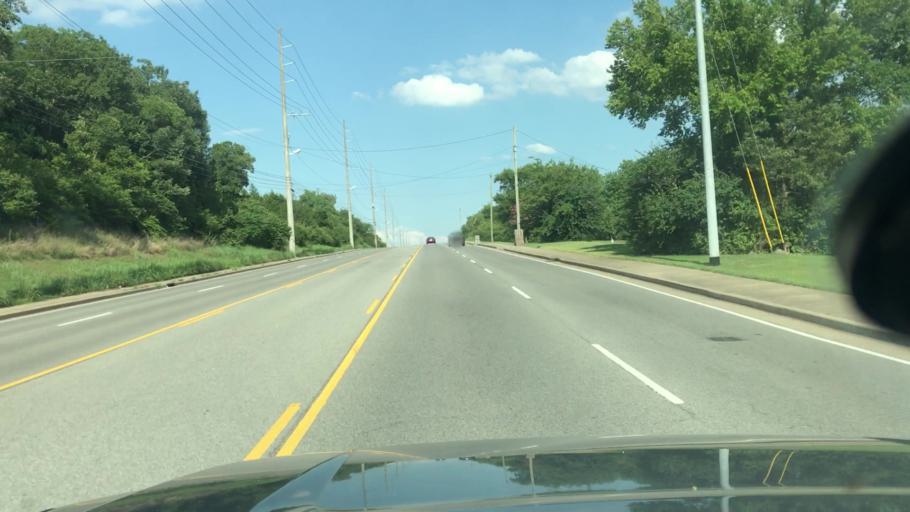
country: US
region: Tennessee
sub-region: Davidson County
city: Nashville
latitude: 36.2071
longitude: -86.8025
